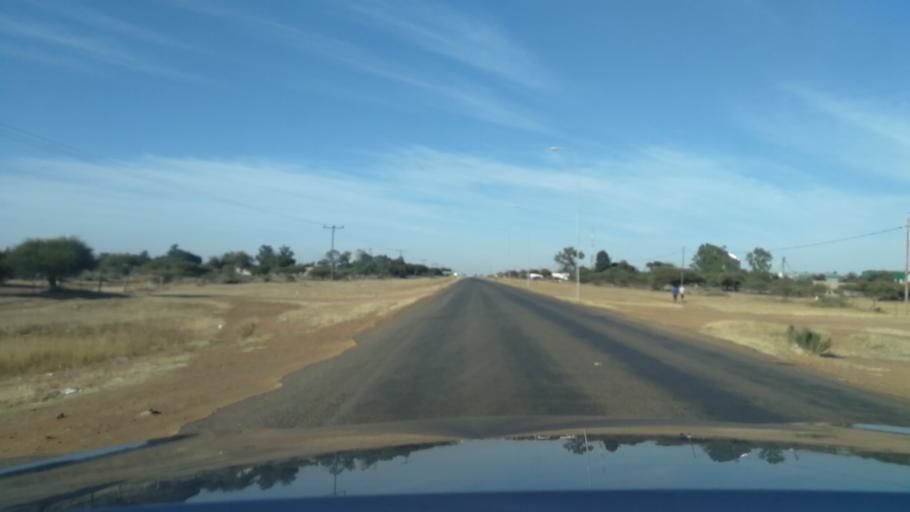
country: BW
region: South East
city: Janeng
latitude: -25.4658
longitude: 25.6010
